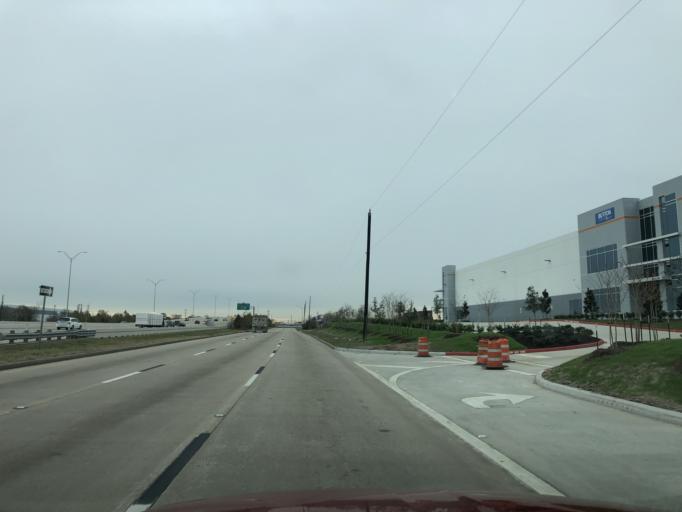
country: US
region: Texas
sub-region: Fort Bend County
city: Missouri City
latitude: 29.6305
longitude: -95.5236
